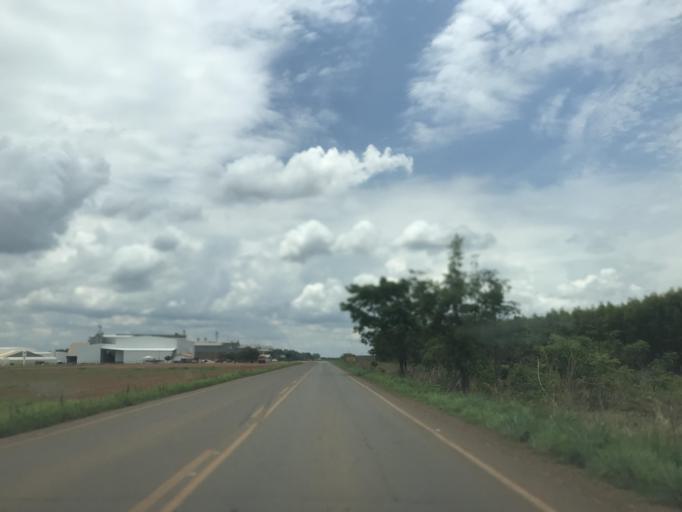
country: BR
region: Goias
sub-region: Vianopolis
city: Vianopolis
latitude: -16.7441
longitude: -48.4639
